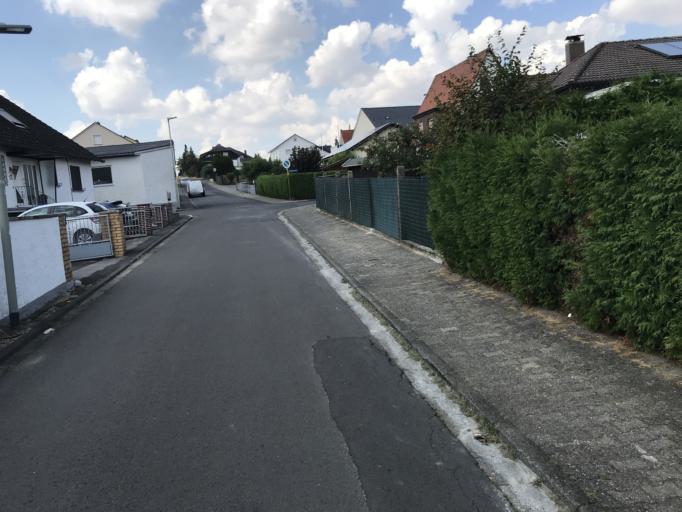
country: DE
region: Hesse
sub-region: Regierungsbezirk Darmstadt
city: Wolfersheim
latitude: 50.3971
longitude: 8.8095
